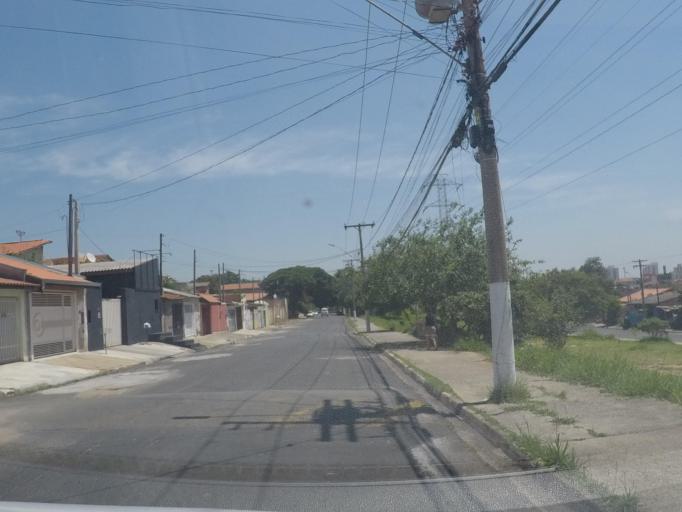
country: BR
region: Sao Paulo
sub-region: Hortolandia
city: Hortolandia
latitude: -22.8556
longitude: -47.1954
